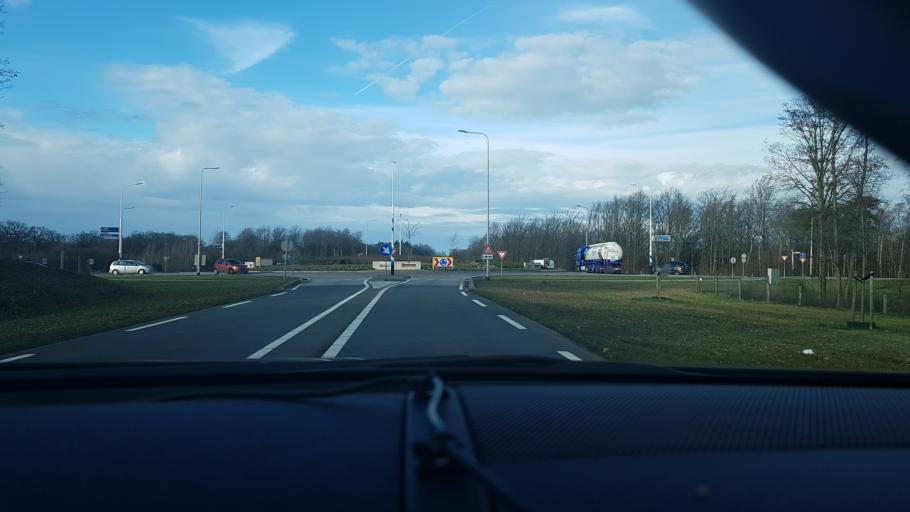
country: NL
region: Limburg
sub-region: Gemeente Peel en Maas
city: Maasbree
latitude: 51.3515
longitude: 6.0145
